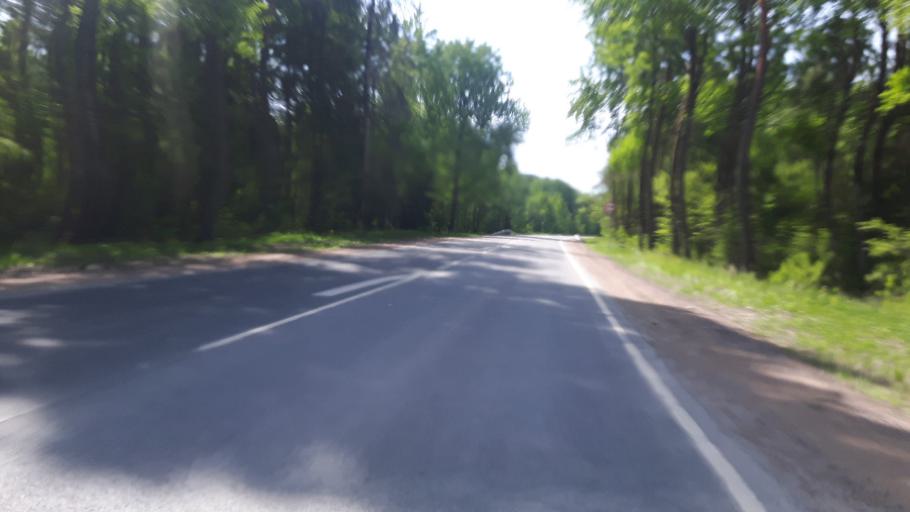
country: RU
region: Leningrad
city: Vistino
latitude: 59.6885
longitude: 28.4610
